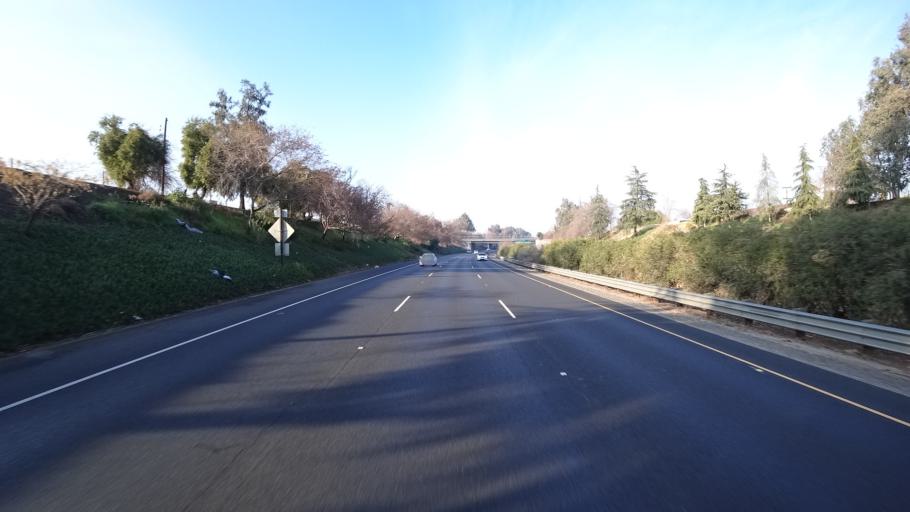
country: US
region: California
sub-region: Kern County
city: Bakersfield
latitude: 35.3839
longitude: -118.9938
